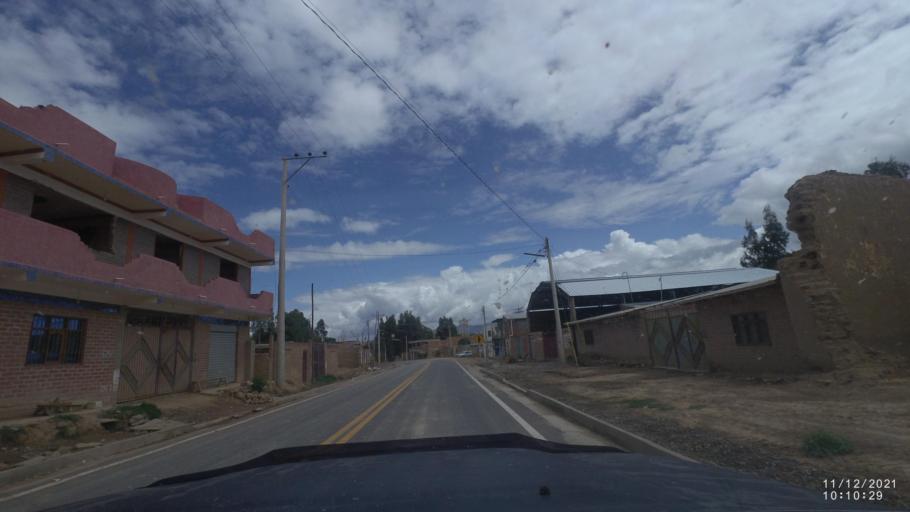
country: BO
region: Cochabamba
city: Tarata
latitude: -17.6444
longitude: -65.9790
